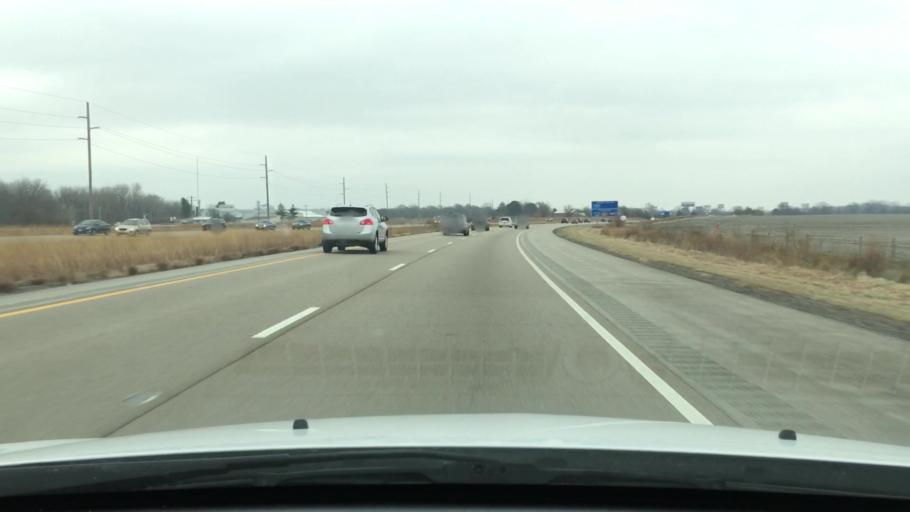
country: US
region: Illinois
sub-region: Logan County
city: Atlanta
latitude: 40.2485
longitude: -89.2449
